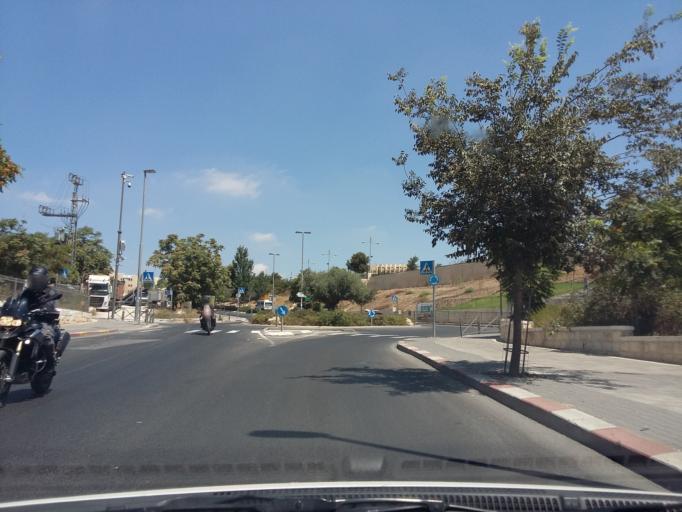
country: PS
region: West Bank
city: East Jerusalem
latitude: 31.7933
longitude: 35.2368
